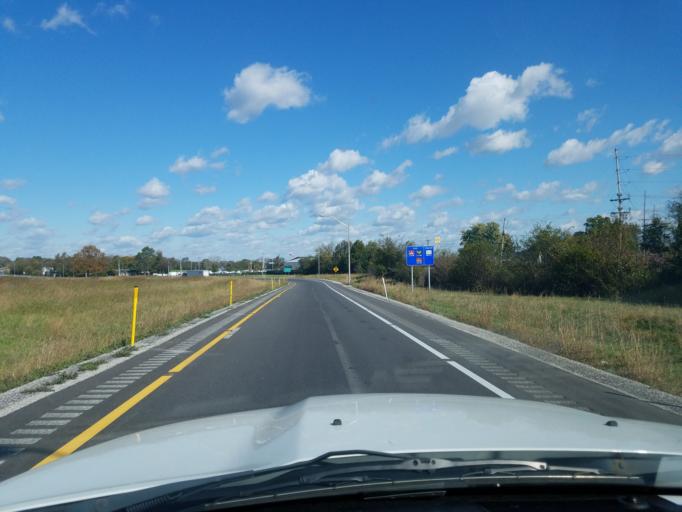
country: US
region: Kentucky
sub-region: Warren County
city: Bowling Green
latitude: 36.9551
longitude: -86.4959
